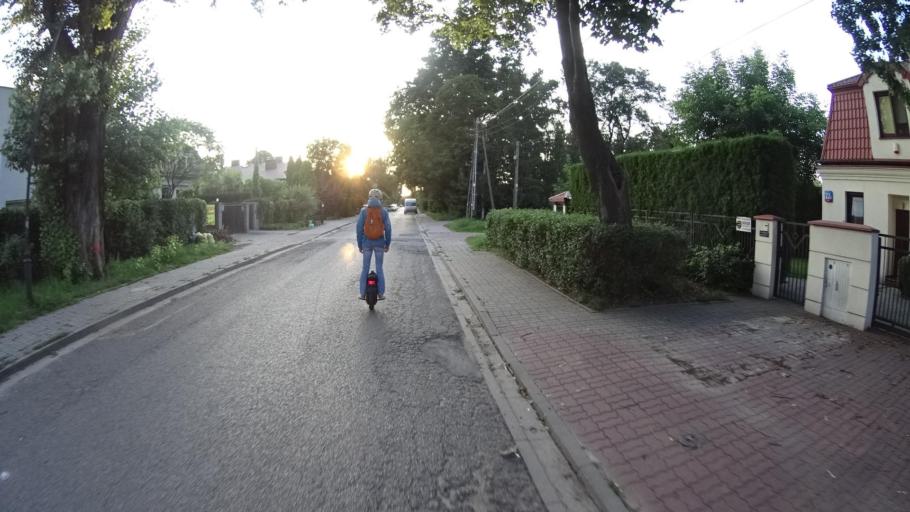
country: PL
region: Masovian Voivodeship
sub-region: Warszawa
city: Bielany
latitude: 52.3054
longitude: 20.9401
